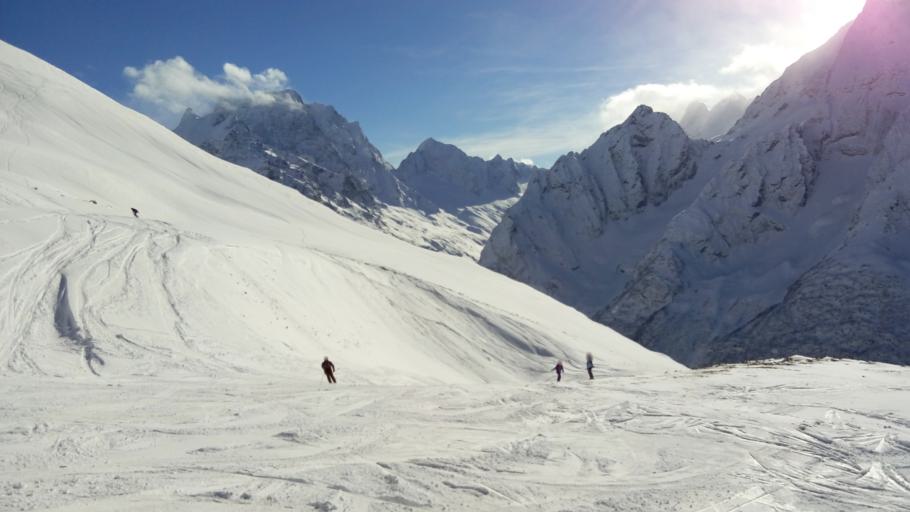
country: RU
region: Karachayevo-Cherkesiya
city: Teberda
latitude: 43.2912
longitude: 41.6619
